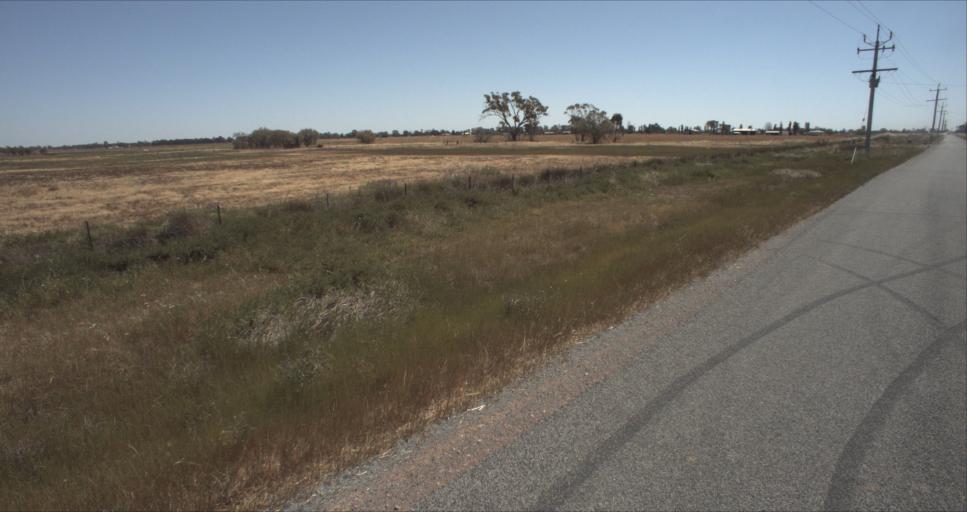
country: AU
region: New South Wales
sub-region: Leeton
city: Leeton
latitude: -34.5159
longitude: 146.4332
